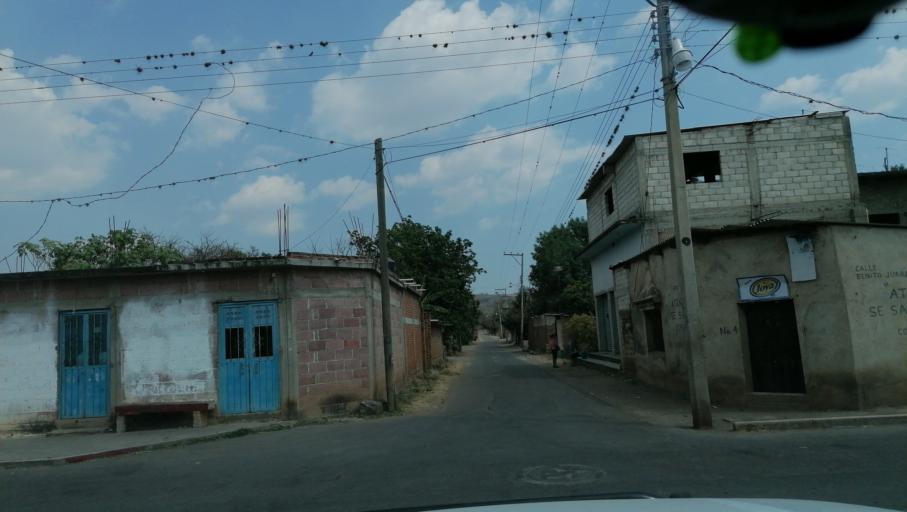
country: MX
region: Puebla
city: San Juan Amecac
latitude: 18.8201
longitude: -98.7048
